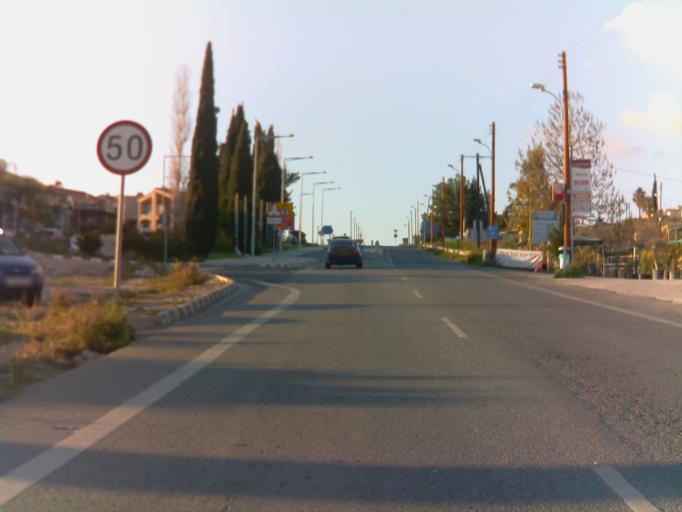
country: CY
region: Pafos
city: Pegeia
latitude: 34.8522
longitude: 32.3823
